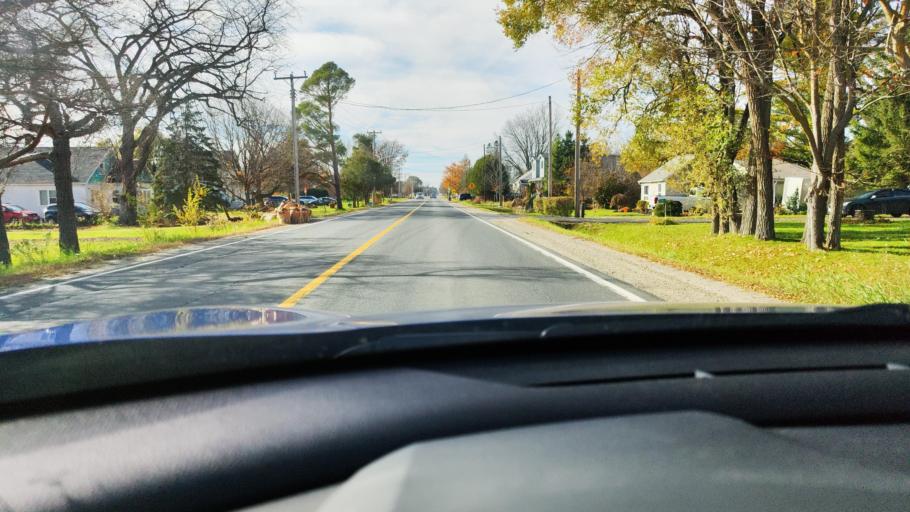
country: CA
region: Ontario
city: Angus
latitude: 44.3601
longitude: -79.9636
